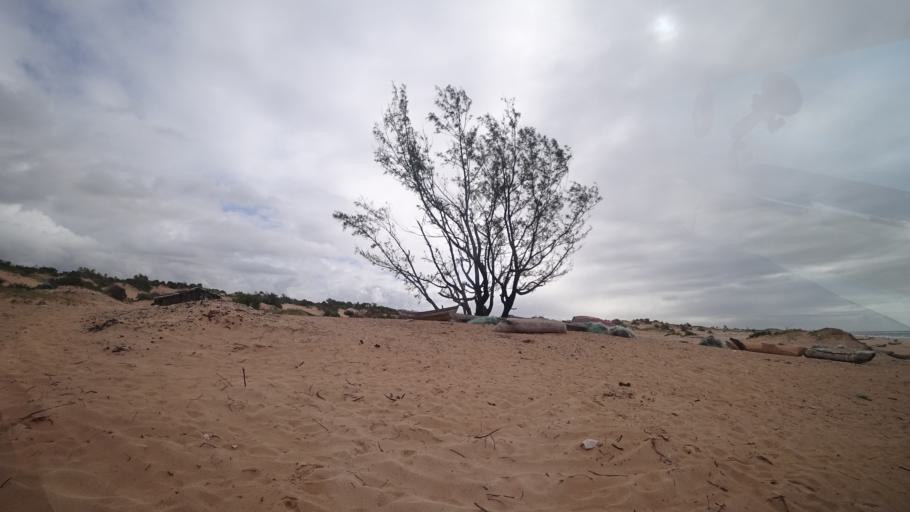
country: MZ
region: Sofala
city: Beira
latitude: -19.6164
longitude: 35.2189
